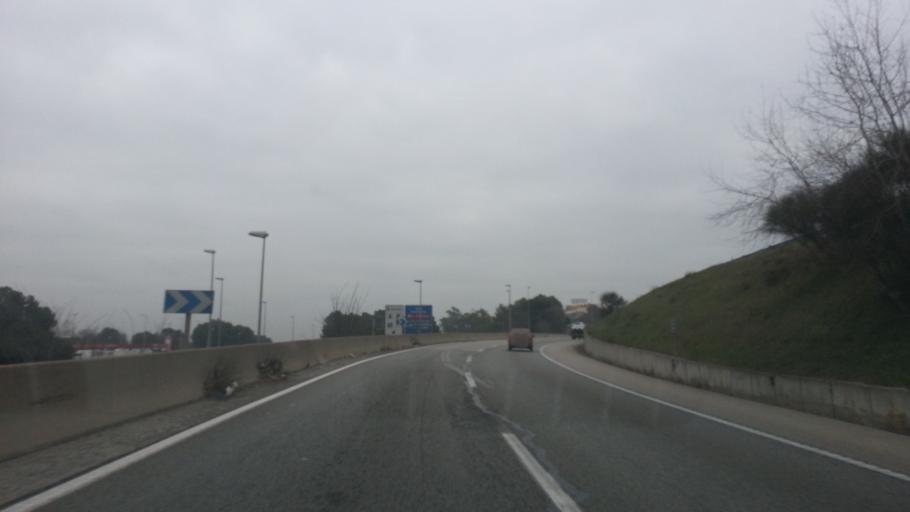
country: ES
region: Catalonia
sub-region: Provincia de Barcelona
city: Sant Cugat del Valles
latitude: 41.4918
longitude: 2.0976
